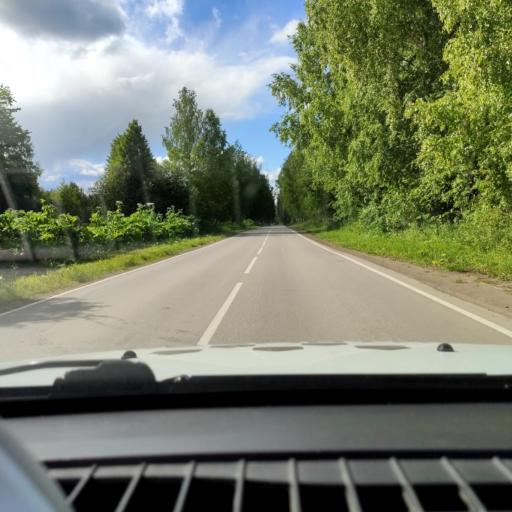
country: RU
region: Perm
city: Overyata
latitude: 58.1025
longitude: 55.8502
